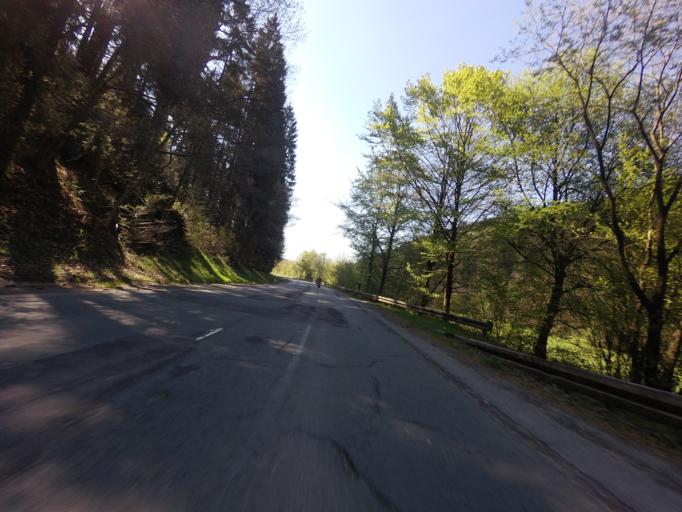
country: DE
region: North Rhine-Westphalia
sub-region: Regierungsbezirk Arnsberg
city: Drolshagen
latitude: 51.0903
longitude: 7.7528
